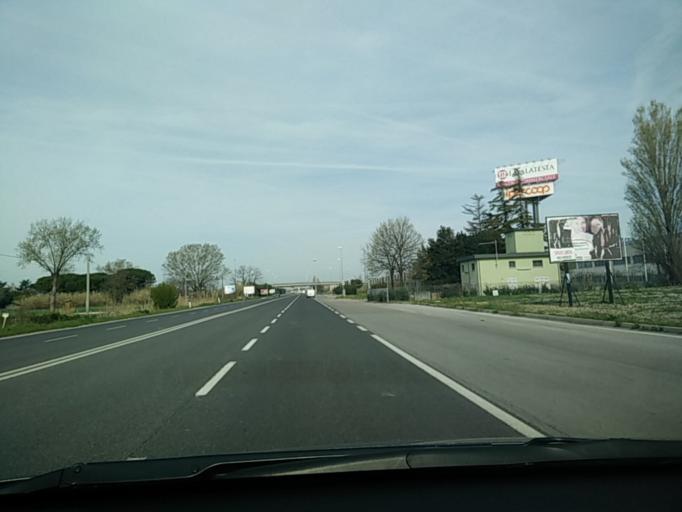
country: IT
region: Emilia-Romagna
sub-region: Provincia di Rimini
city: Rimini
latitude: 44.0663
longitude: 12.5292
